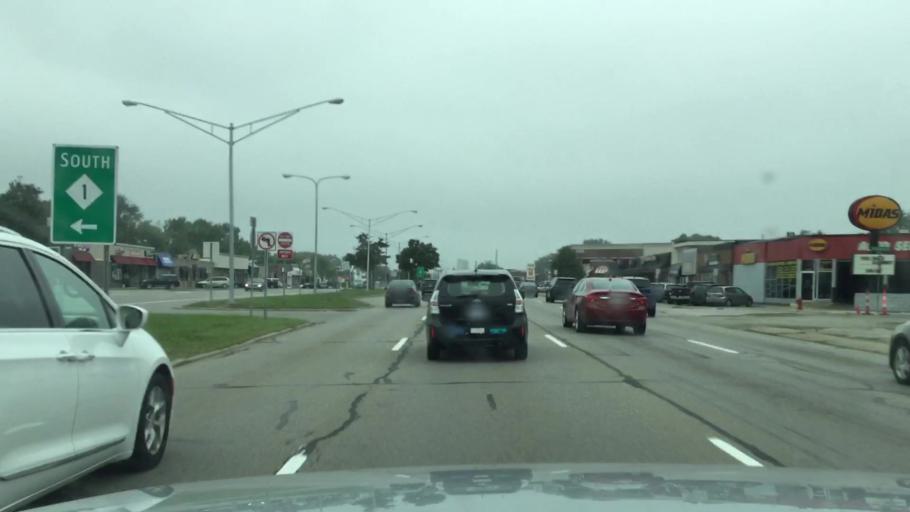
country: US
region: Michigan
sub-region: Oakland County
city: Birmingham
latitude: 42.5291
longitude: -83.1969
